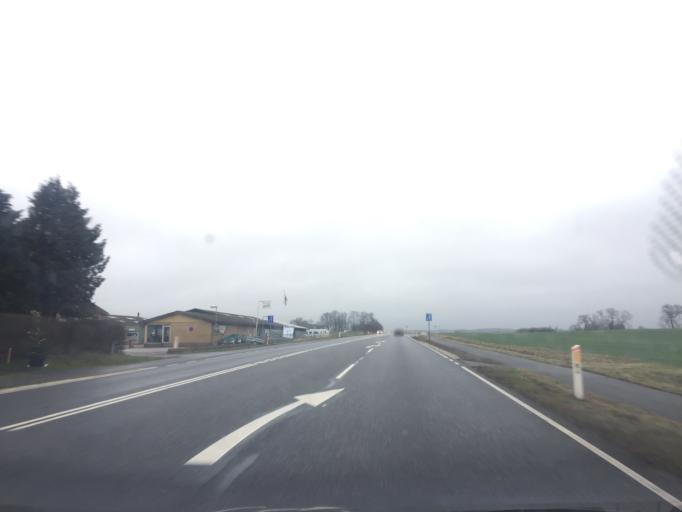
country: DK
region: Zealand
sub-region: Slagelse Kommune
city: Slagelse
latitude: 55.4220
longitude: 11.4321
